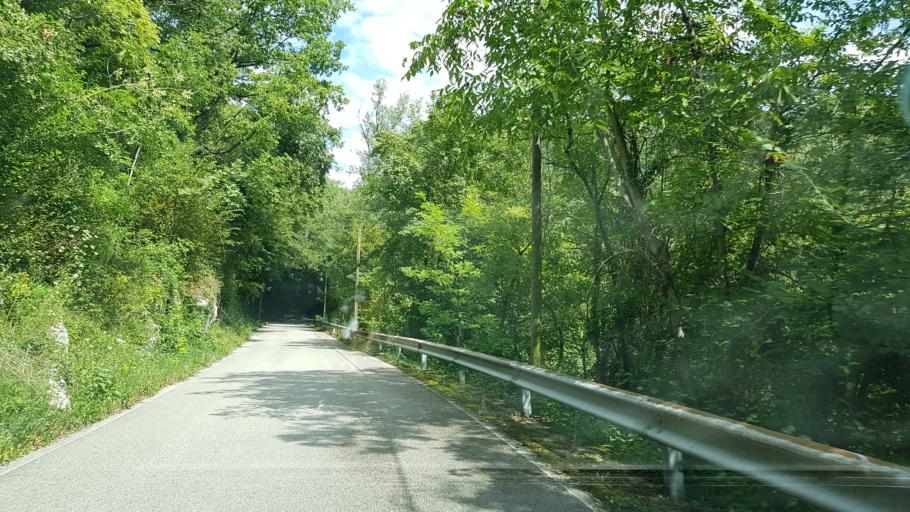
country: IT
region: Friuli Venezia Giulia
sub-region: Provincia di Udine
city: Prepotto
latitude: 46.0672
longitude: 13.5244
